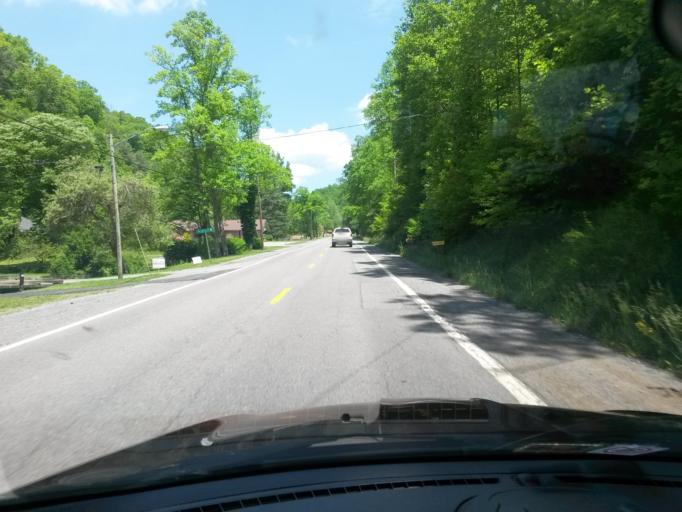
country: US
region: West Virginia
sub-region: McDowell County
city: Welch
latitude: 37.4671
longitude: -81.5412
